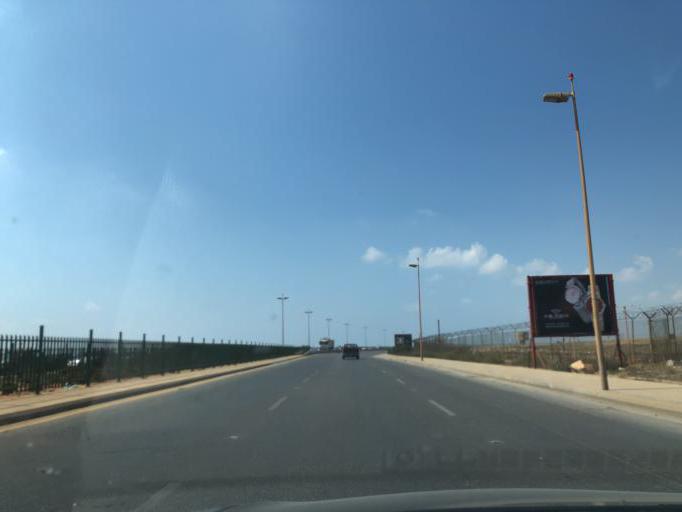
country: LB
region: Mont-Liban
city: Baabda
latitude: 33.7943
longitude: 35.4788
